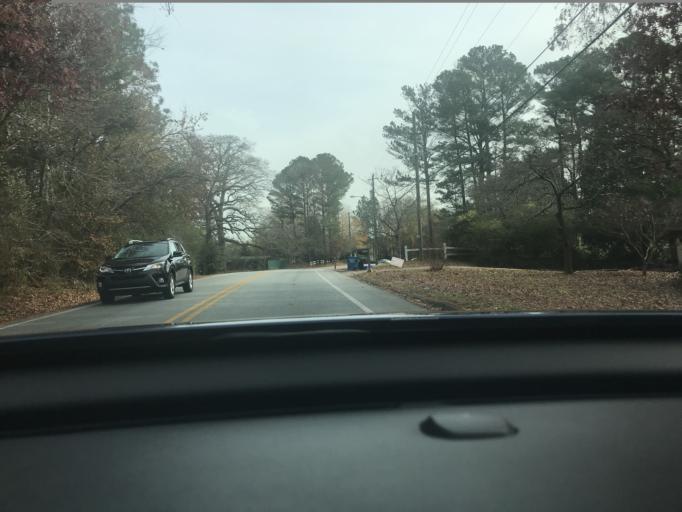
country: US
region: Georgia
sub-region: Gwinnett County
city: Lilburn
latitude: 33.8979
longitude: -84.0993
